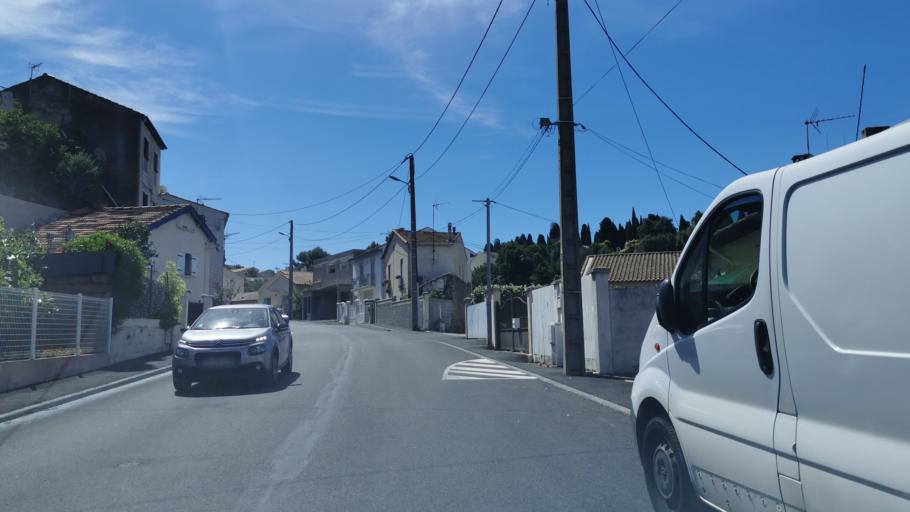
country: FR
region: Languedoc-Roussillon
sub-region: Departement de l'Herault
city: Beziers
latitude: 43.3531
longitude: 3.2133
